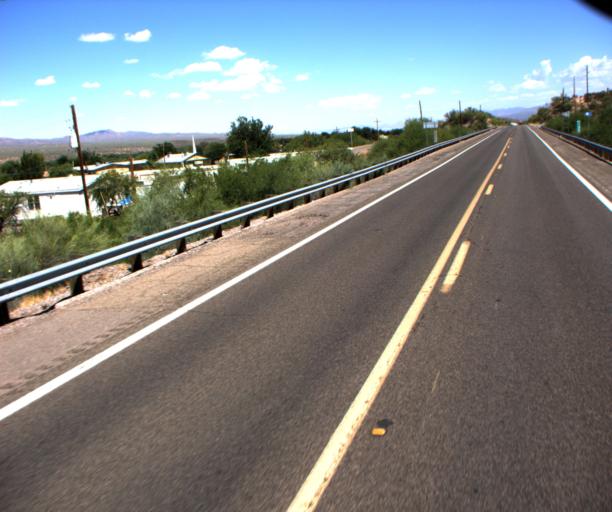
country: US
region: Arizona
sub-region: Pinal County
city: Mammoth
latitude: 32.9157
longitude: -110.7210
